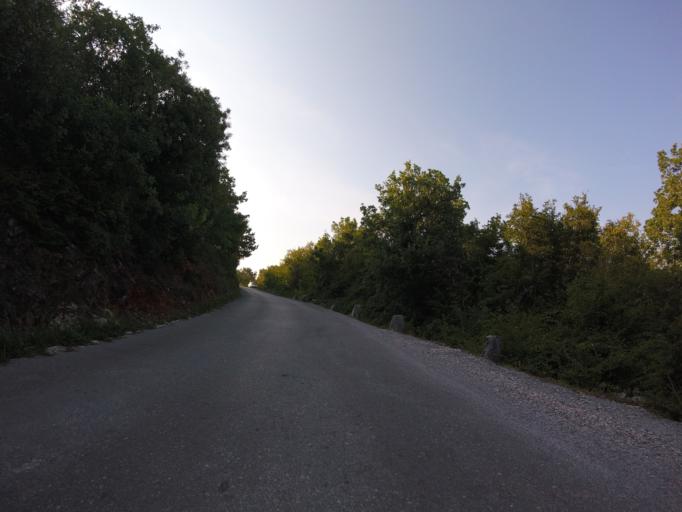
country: HR
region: Primorsko-Goranska
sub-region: Grad Crikvenica
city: Crikvenica
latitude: 45.1918
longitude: 14.7192
